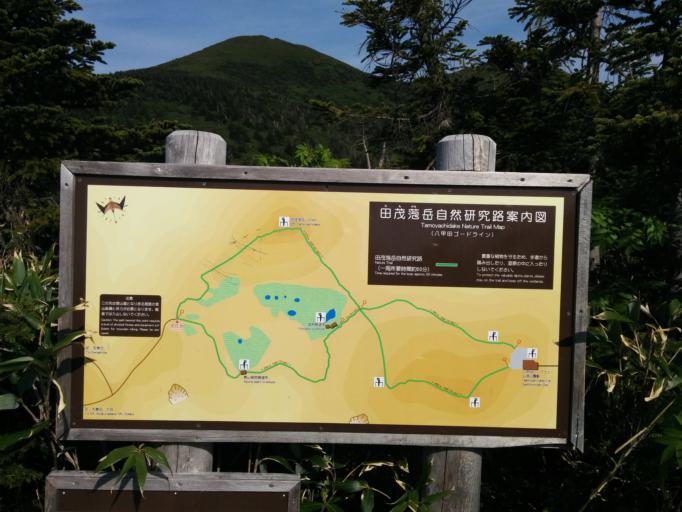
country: JP
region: Aomori
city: Aomori Shi
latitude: 40.6735
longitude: 140.8674
